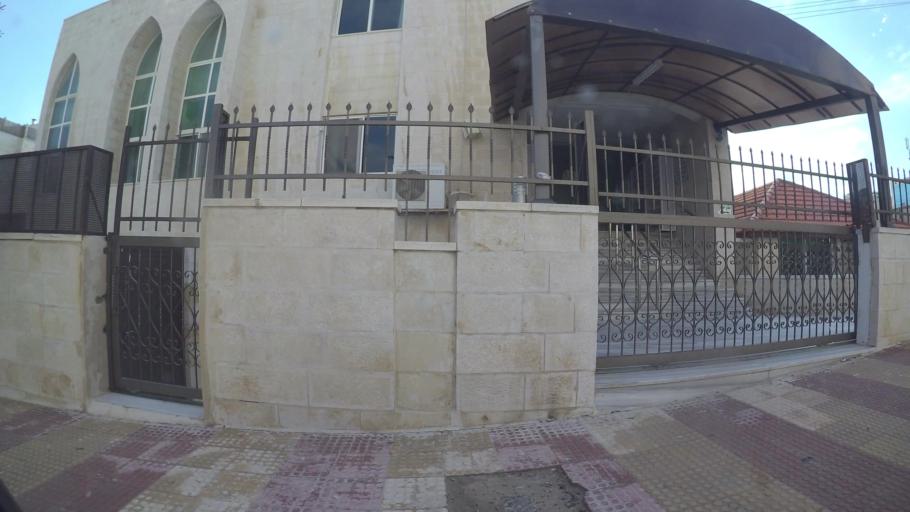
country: JO
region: Amman
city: Al Jubayhah
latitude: 32.0021
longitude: 35.8644
